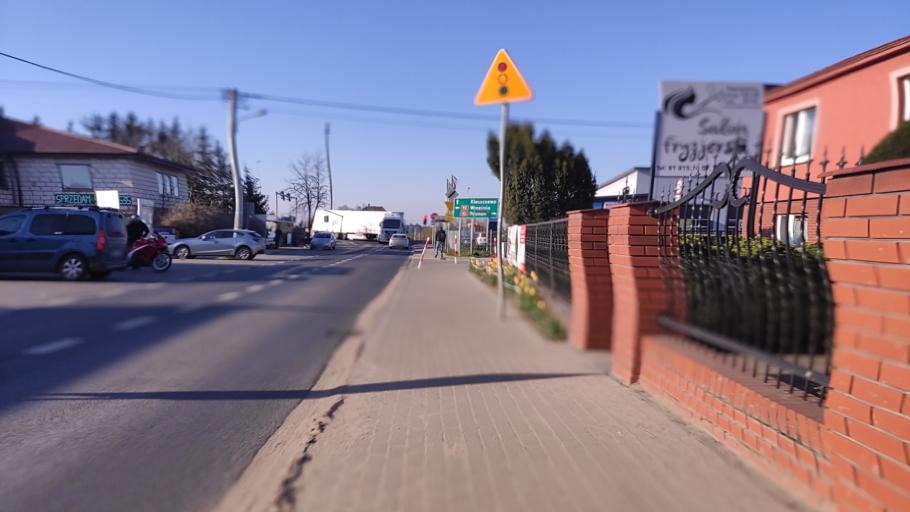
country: PL
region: Greater Poland Voivodeship
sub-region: Powiat poznanski
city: Kleszczewo
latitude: 52.3994
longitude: 17.1587
